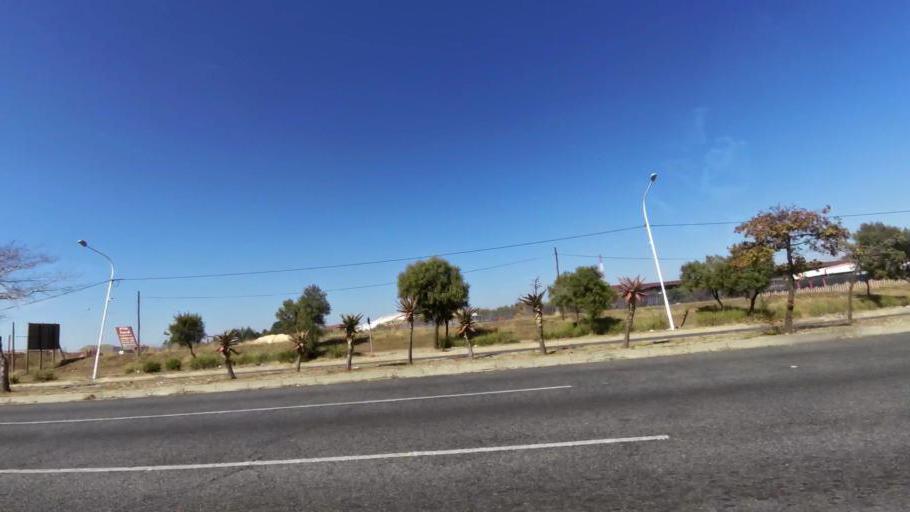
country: ZA
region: Gauteng
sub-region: City of Johannesburg Metropolitan Municipality
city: Johannesburg
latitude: -26.2485
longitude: 27.9757
